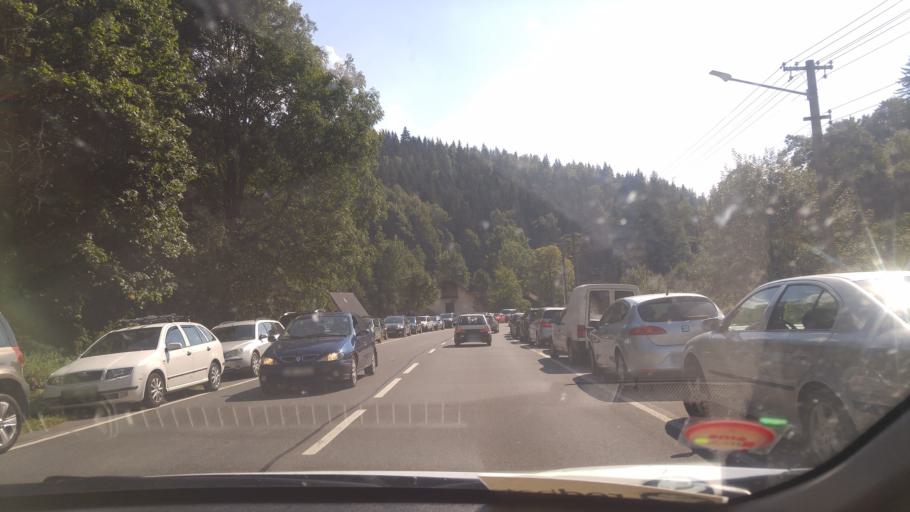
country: CZ
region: Olomoucky
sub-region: Okres Sumperk
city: Stare Mesto
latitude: 50.1471
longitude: 17.0140
